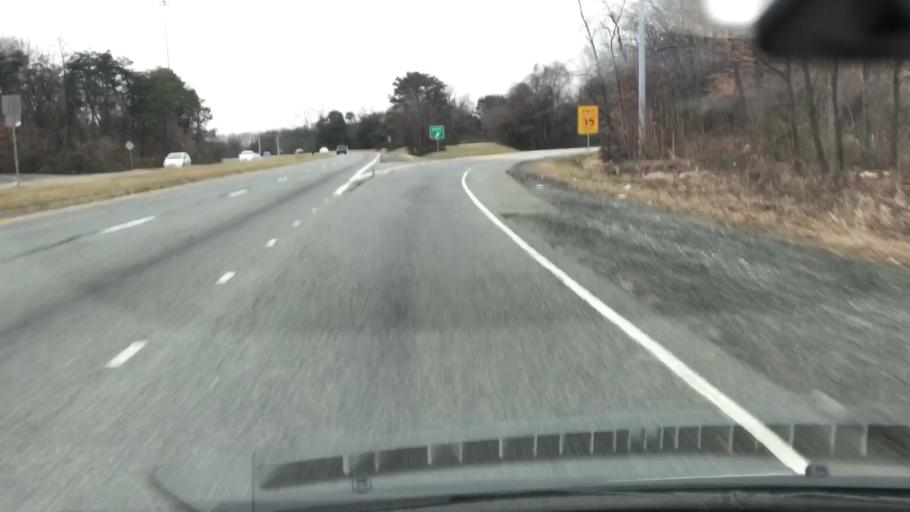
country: US
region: Virginia
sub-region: Prince William County
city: Potomac Mills
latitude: 38.6267
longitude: -77.2890
